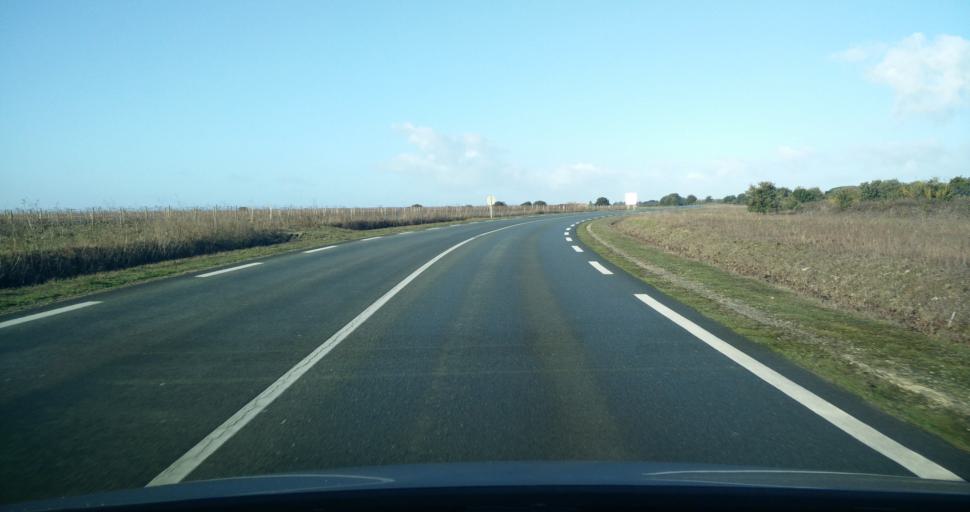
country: FR
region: Poitou-Charentes
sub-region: Departement de la Charente-Maritime
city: Rivedoux-Plage
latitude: 46.1527
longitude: -1.2834
